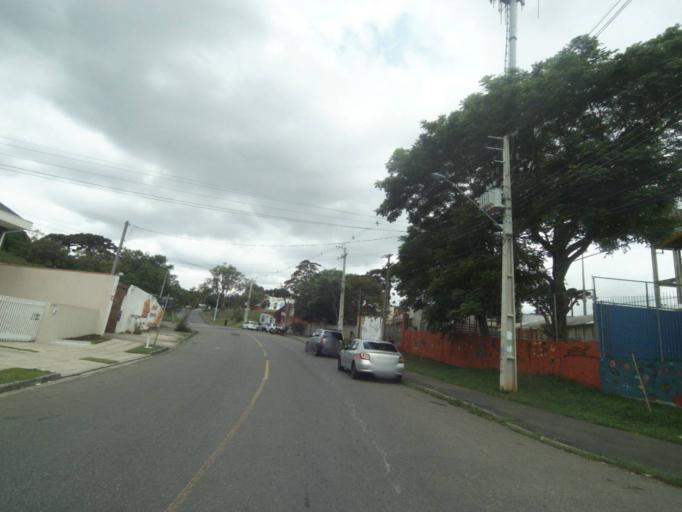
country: BR
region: Parana
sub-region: Curitiba
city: Curitiba
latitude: -25.3882
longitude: -49.2847
